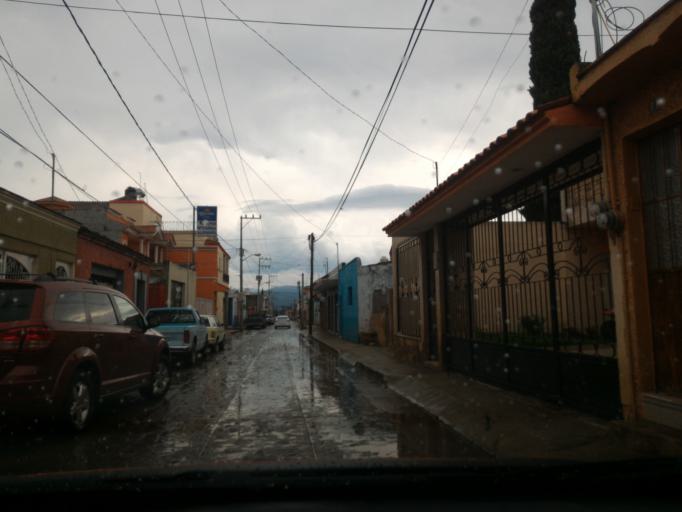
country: MX
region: Jalisco
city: San Andres Ixtlan
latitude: 19.8202
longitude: -103.4665
